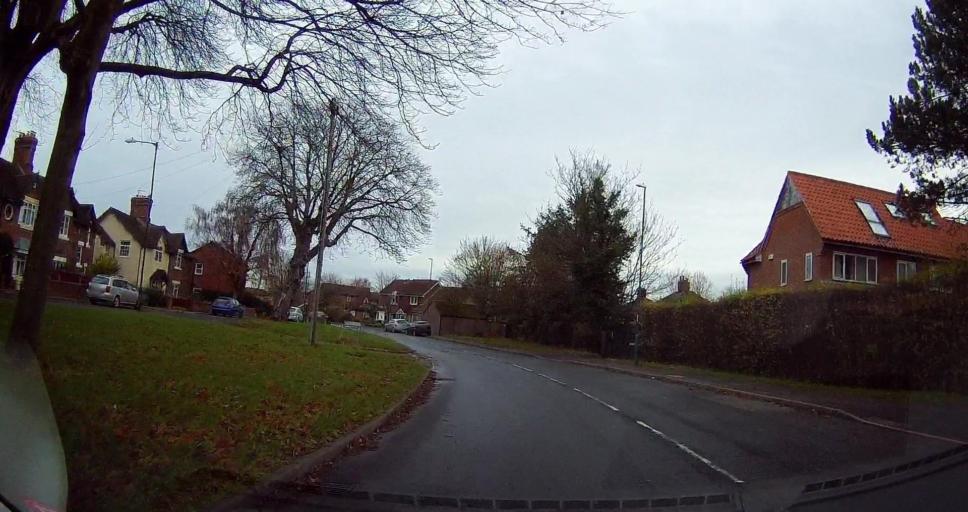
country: GB
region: England
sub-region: Nottinghamshire
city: Kimberley
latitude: 52.9560
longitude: -1.2271
